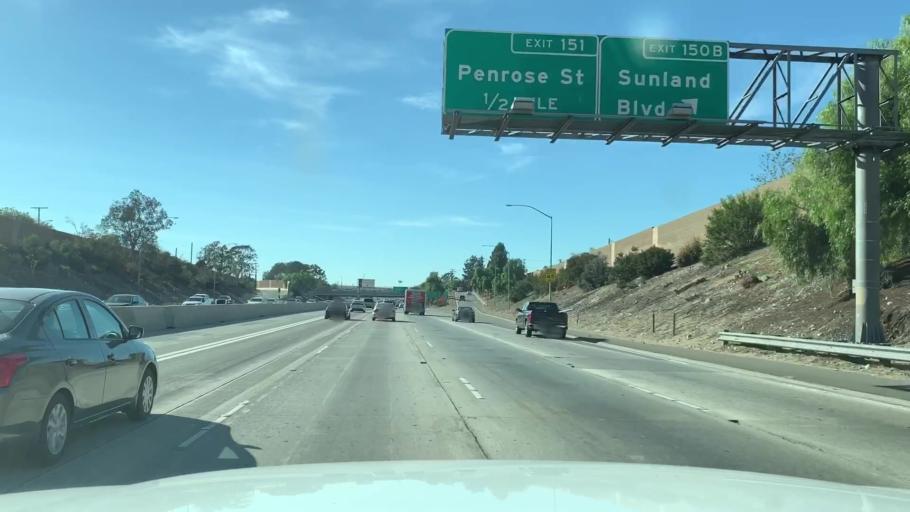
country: US
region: California
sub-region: Los Angeles County
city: North Hollywood
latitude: 34.2219
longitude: -118.3624
